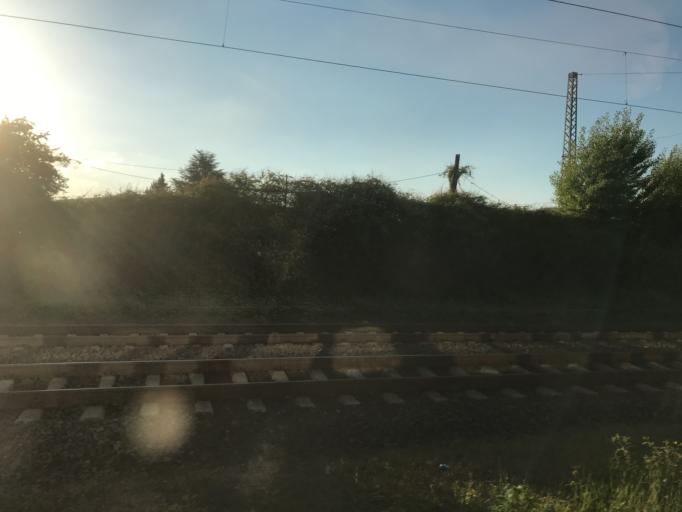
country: DE
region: Rheinland-Pfalz
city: Gartenstadt
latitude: 49.4586
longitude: 8.4188
